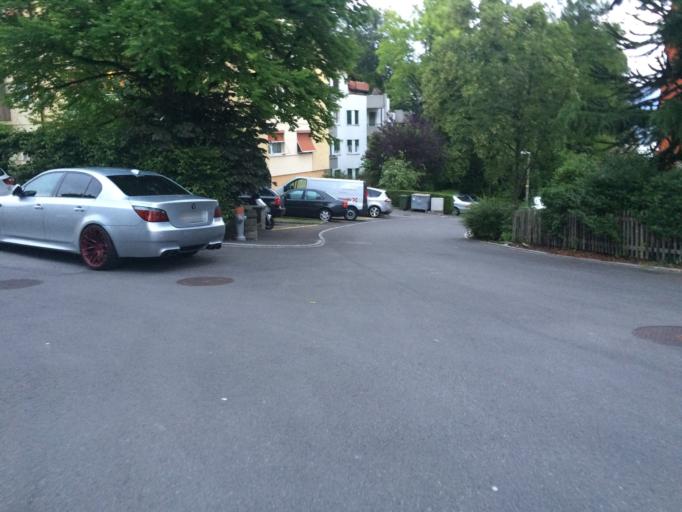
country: CH
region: Zurich
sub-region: Bezirk Horgen
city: Horgen / Oberdorf
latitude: 47.2582
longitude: 8.5916
